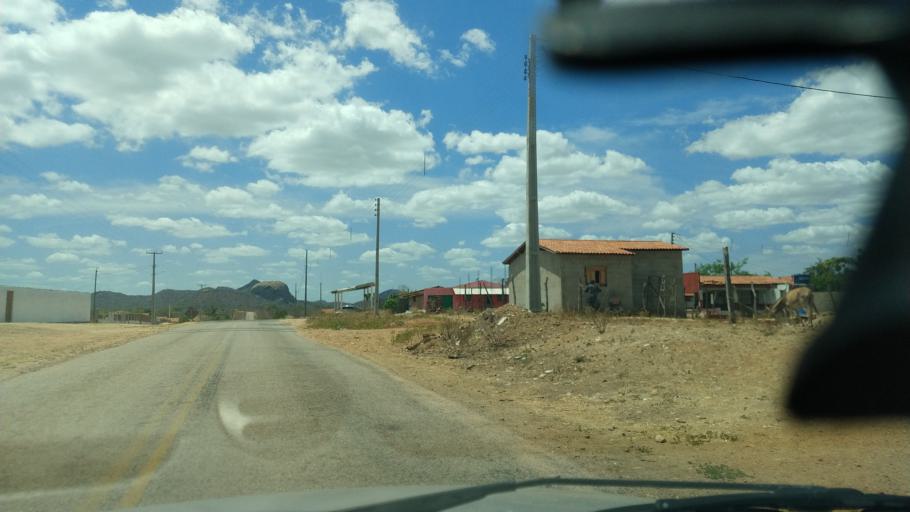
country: BR
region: Rio Grande do Norte
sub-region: Sao Paulo Do Potengi
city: Sao Paulo do Potengi
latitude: -5.9661
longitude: -35.8891
